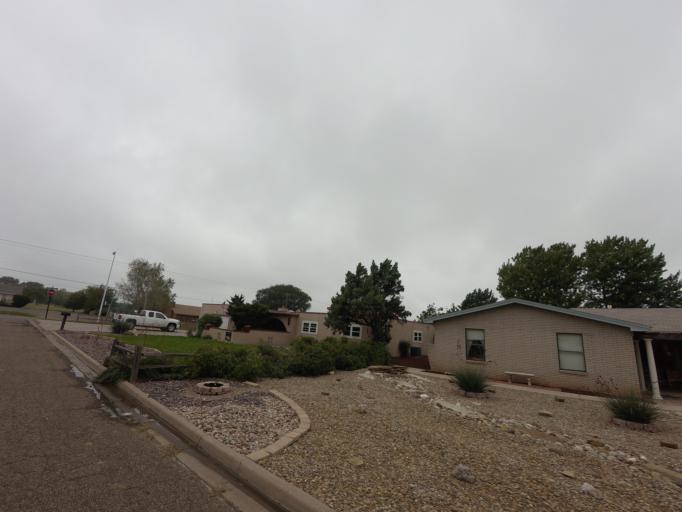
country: US
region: New Mexico
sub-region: Curry County
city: Clovis
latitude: 34.4343
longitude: -103.1882
